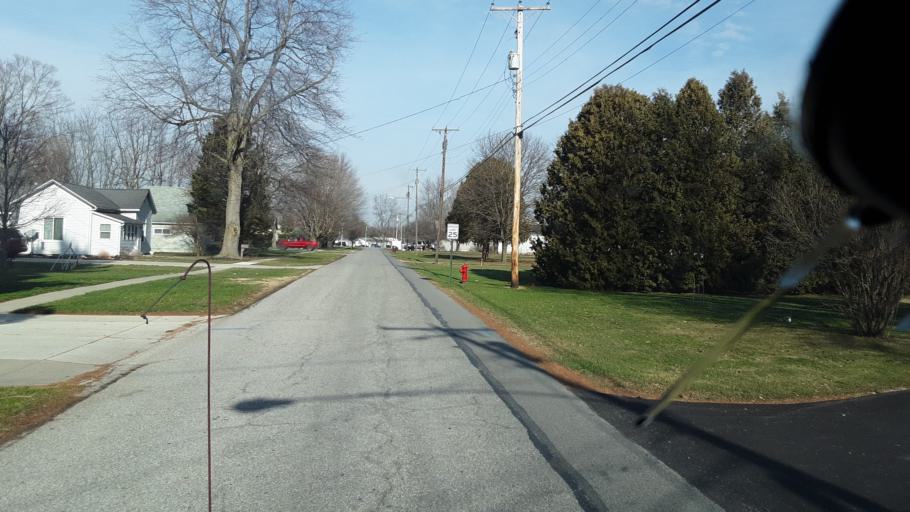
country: US
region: Ohio
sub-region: Defiance County
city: Hicksville
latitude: 41.2915
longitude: -84.7731
